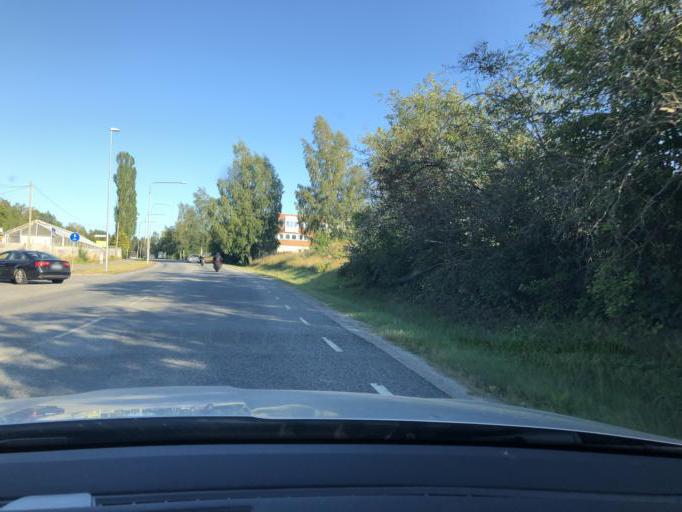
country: SE
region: Stockholm
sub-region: Sodertalje Kommun
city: Soedertaelje
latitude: 59.1837
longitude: 17.5940
